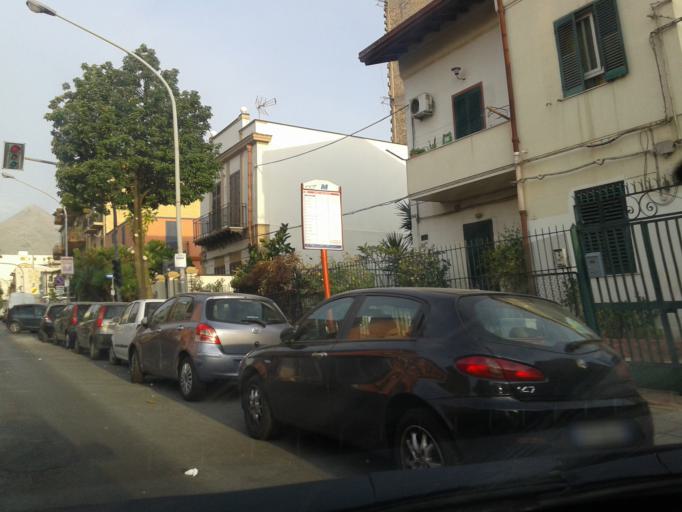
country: IT
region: Sicily
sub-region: Palermo
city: Palermo
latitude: 38.1105
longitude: 13.3315
